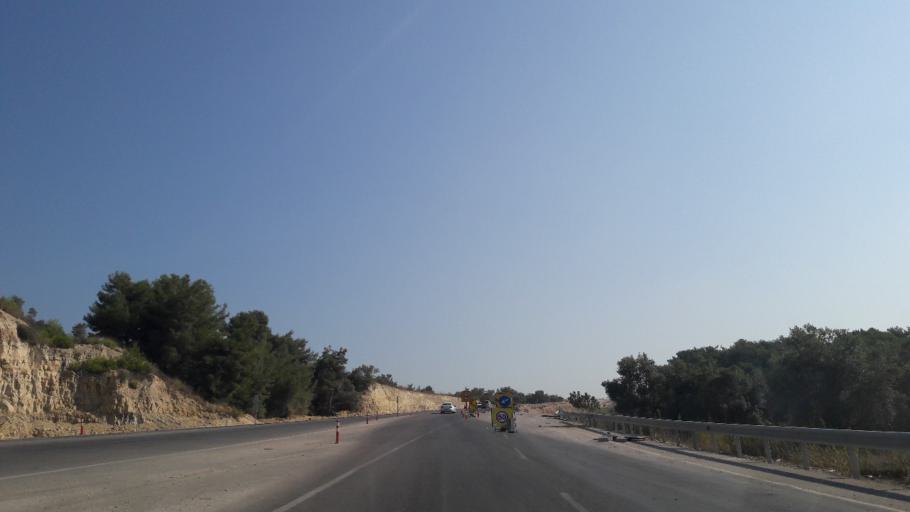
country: TR
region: Adana
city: Yuregir
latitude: 37.0802
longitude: 35.4742
